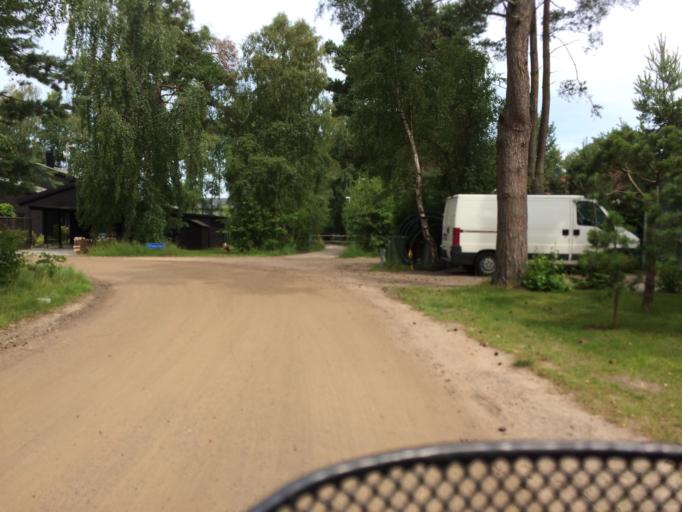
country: SE
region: Skane
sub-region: Vellinge Kommun
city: Ljunghusen
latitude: 55.4043
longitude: 12.9255
